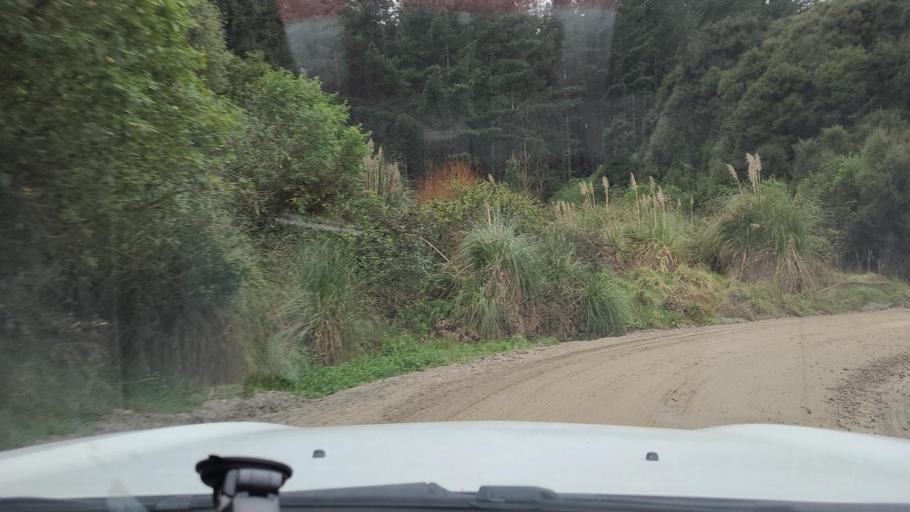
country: NZ
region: Gisborne
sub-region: Gisborne District
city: Gisborne
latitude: -38.5764
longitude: 178.0249
